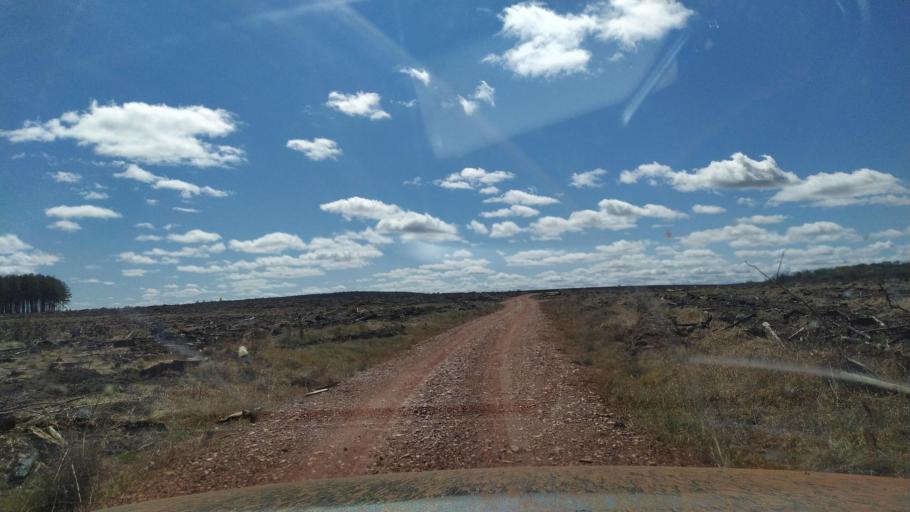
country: AR
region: Corrientes
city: Gobernador Ingeniero Valentin Virasoro
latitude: -28.2973
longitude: -56.0534
